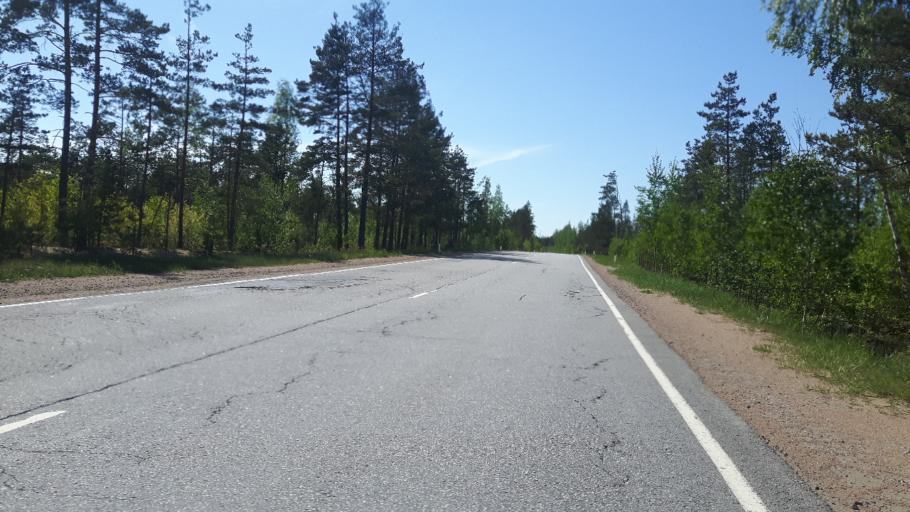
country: RU
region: Leningrad
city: Sista-Palkino
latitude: 59.7695
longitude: 28.7869
